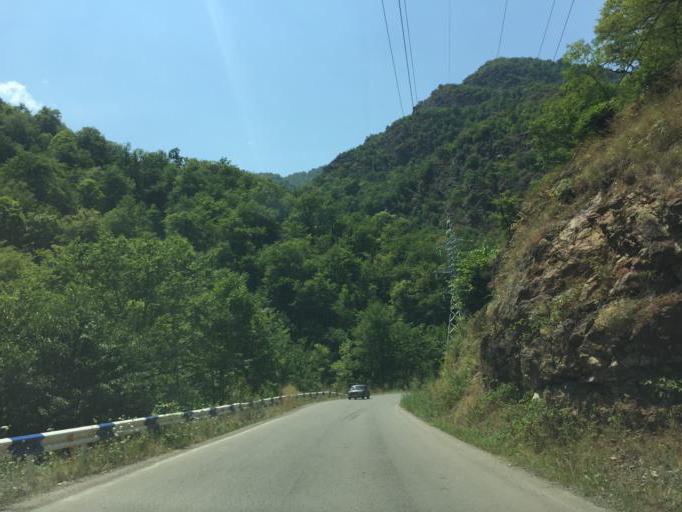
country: AZ
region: Kalbacar Rayonu
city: Kerbakhiar
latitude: 40.1244
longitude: 46.4055
